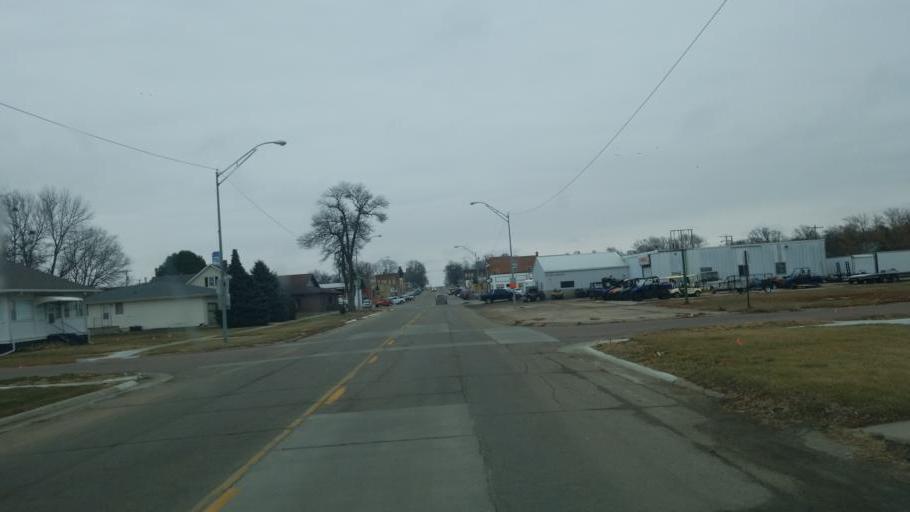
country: US
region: Nebraska
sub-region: Knox County
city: Bloomfield
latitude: 42.5992
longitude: -97.6488
